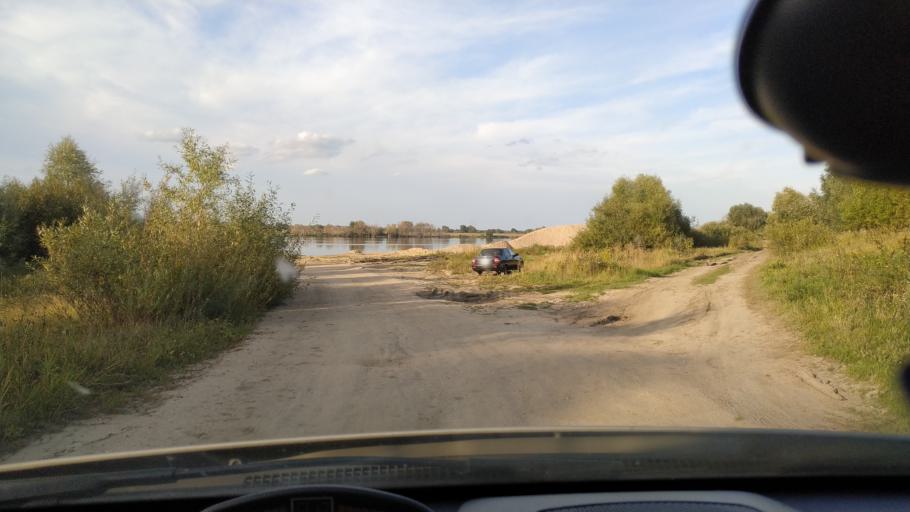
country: RU
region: Rjazan
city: Rybnoye
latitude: 54.8712
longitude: 39.6527
